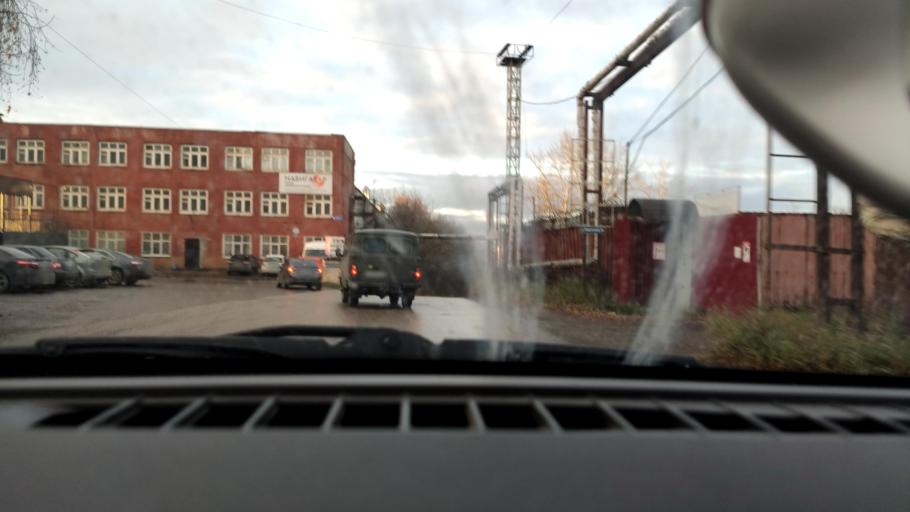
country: RU
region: Perm
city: Kondratovo
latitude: 57.9601
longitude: 56.1550
